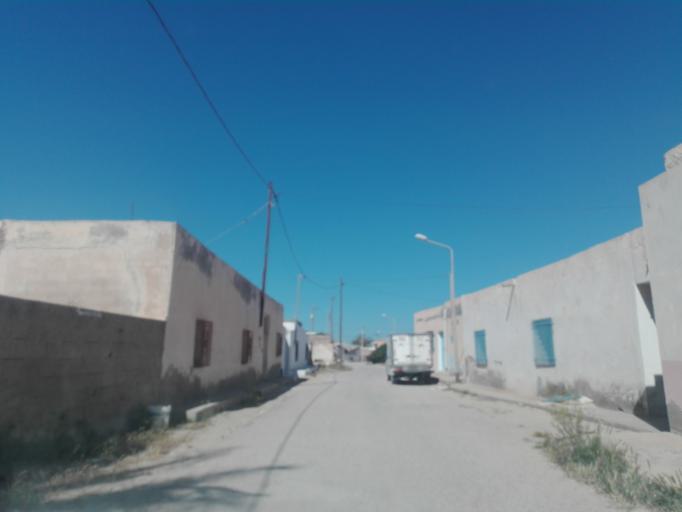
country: TN
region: Safaqis
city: Al Qarmadah
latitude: 34.7132
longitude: 11.1957
